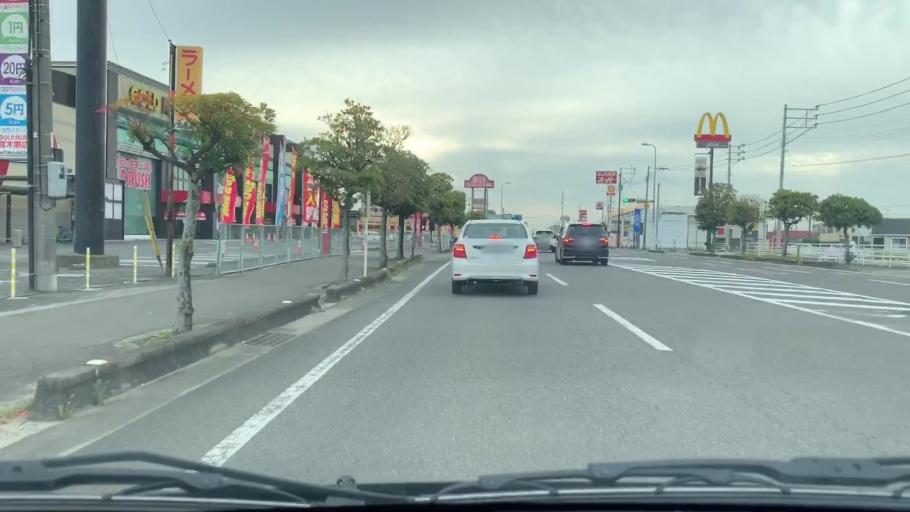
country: JP
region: Saga Prefecture
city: Saga-shi
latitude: 33.2937
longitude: 130.2846
